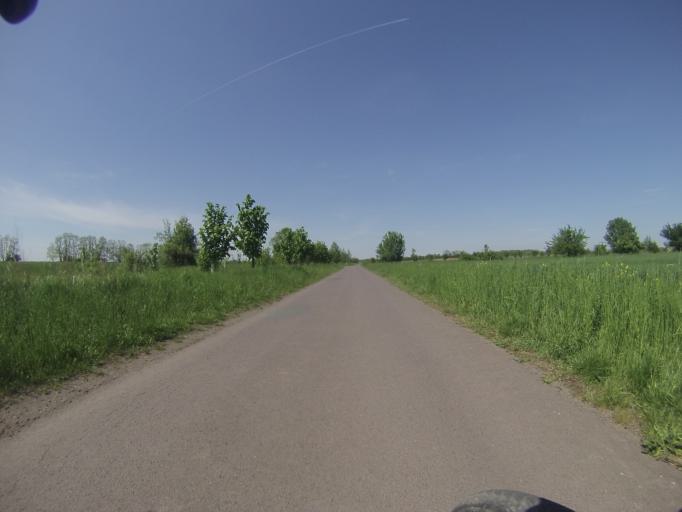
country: CZ
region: South Moravian
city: Novosedly
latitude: 48.8058
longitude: 16.4869
